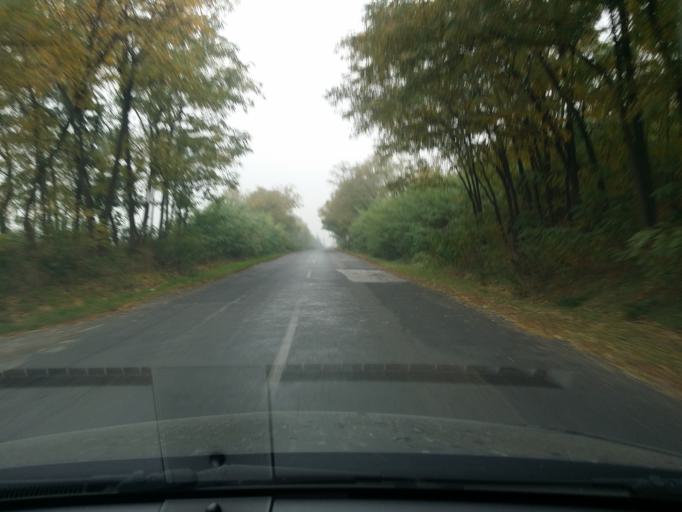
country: HU
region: Szabolcs-Szatmar-Bereg
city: Nyirbogdany
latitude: 48.0727
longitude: 21.8596
